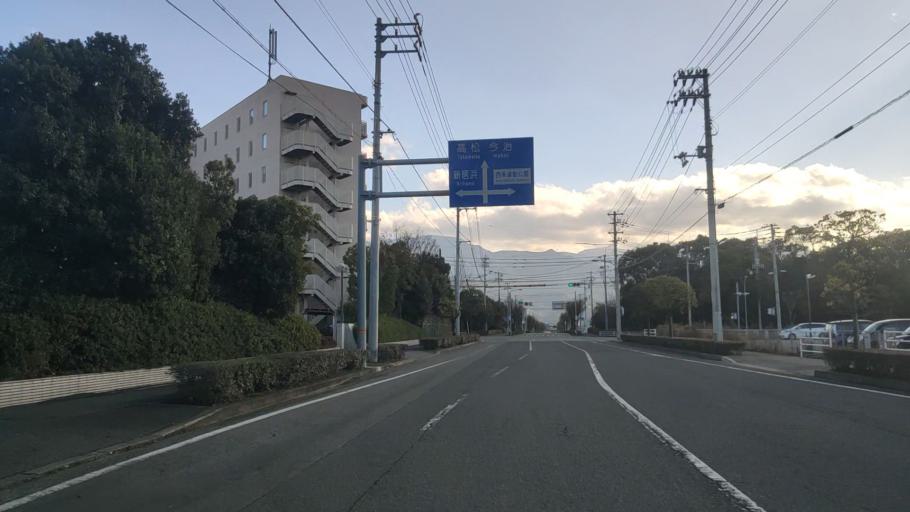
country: JP
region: Ehime
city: Saijo
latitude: 33.9361
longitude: 133.1923
